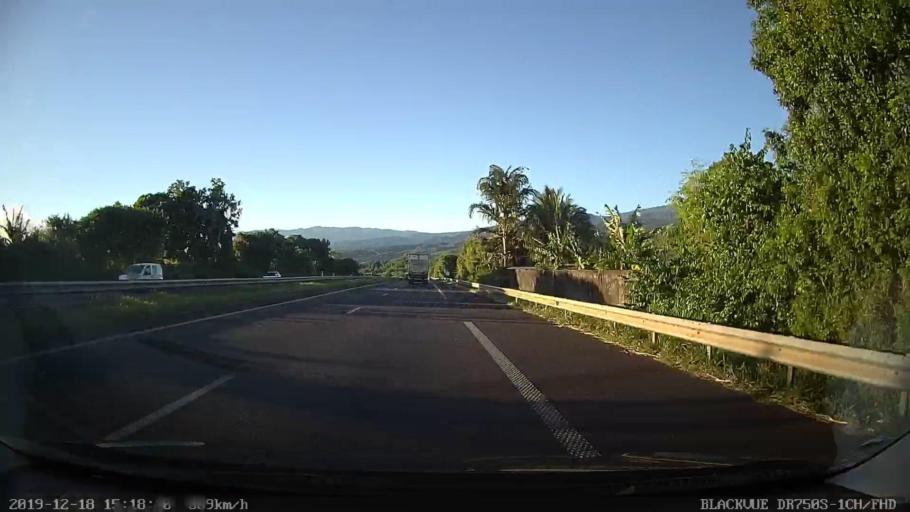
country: RE
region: Reunion
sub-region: Reunion
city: Saint-Andre
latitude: -20.9763
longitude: 55.6543
